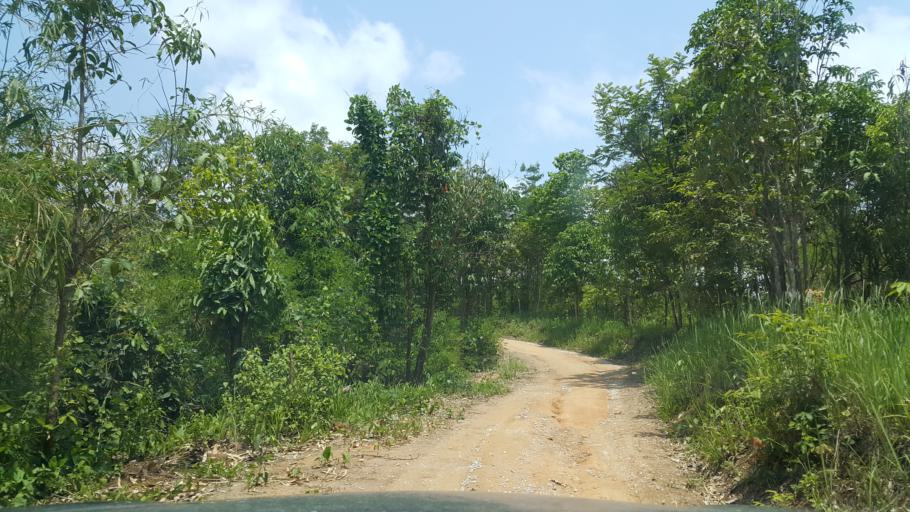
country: TH
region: Chiang Rai
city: Chiang Rai
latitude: 19.9994
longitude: 99.7174
